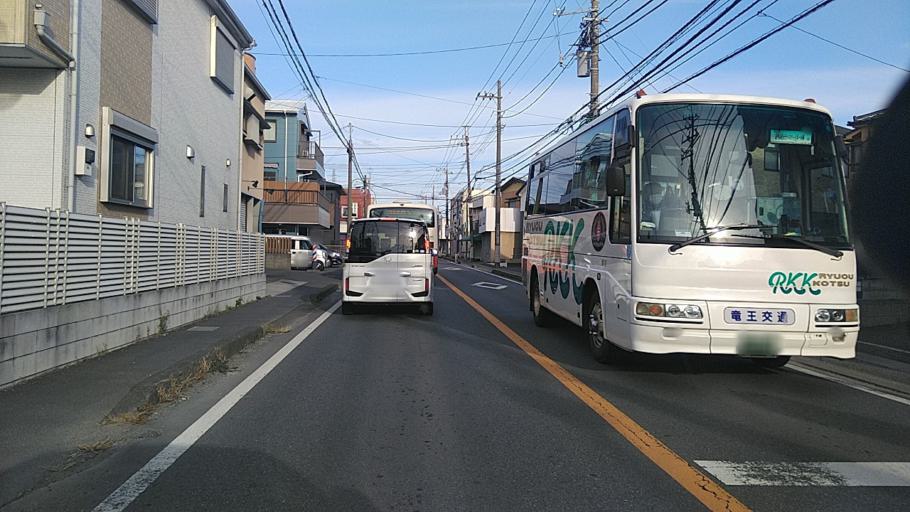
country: JP
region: Chiba
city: Abiko
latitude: 35.8842
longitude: 139.9917
